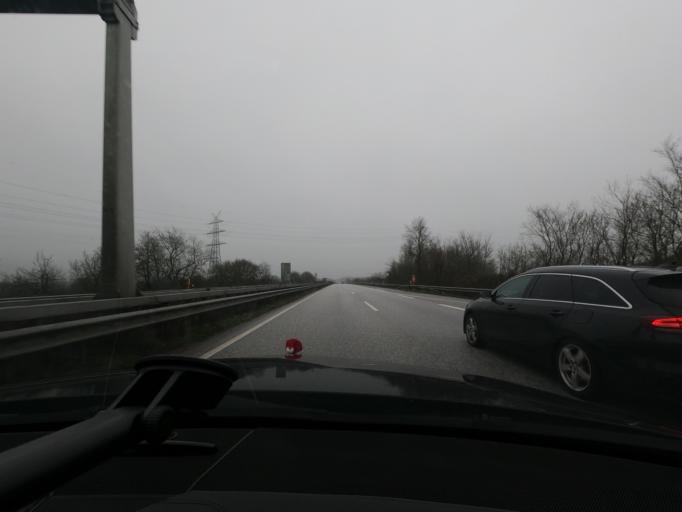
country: DE
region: Schleswig-Holstein
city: Schulldorf
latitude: 54.2993
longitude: 9.7589
